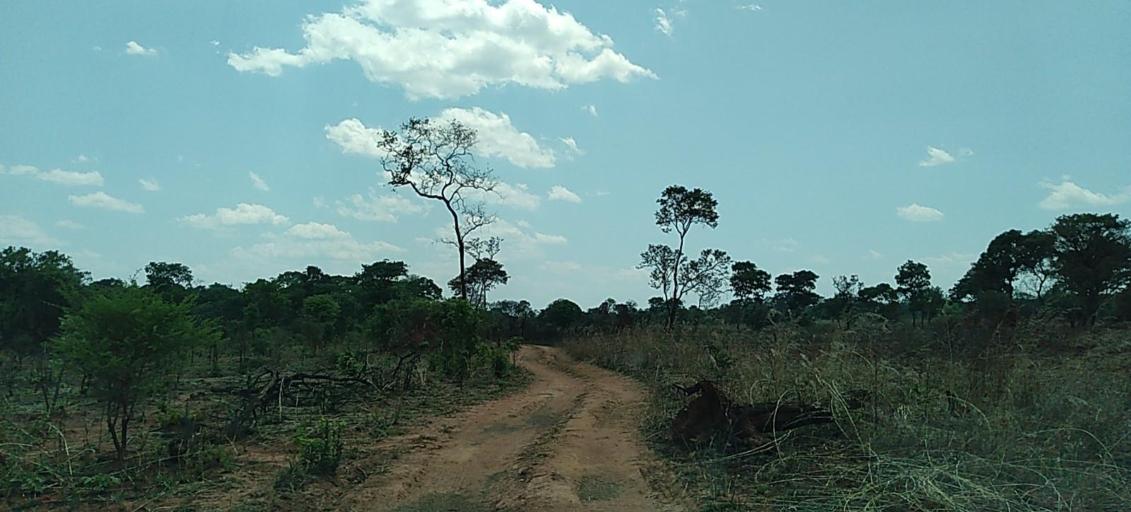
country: ZM
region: Central
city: Kapiri Mposhi
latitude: -13.6308
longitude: 28.7690
